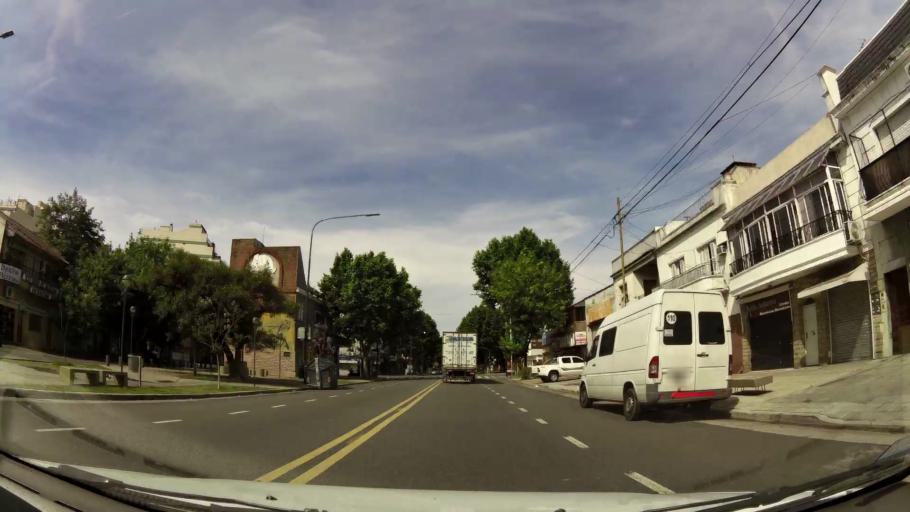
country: AR
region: Buenos Aires F.D.
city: Villa Lugano
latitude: -34.6518
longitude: -58.5150
